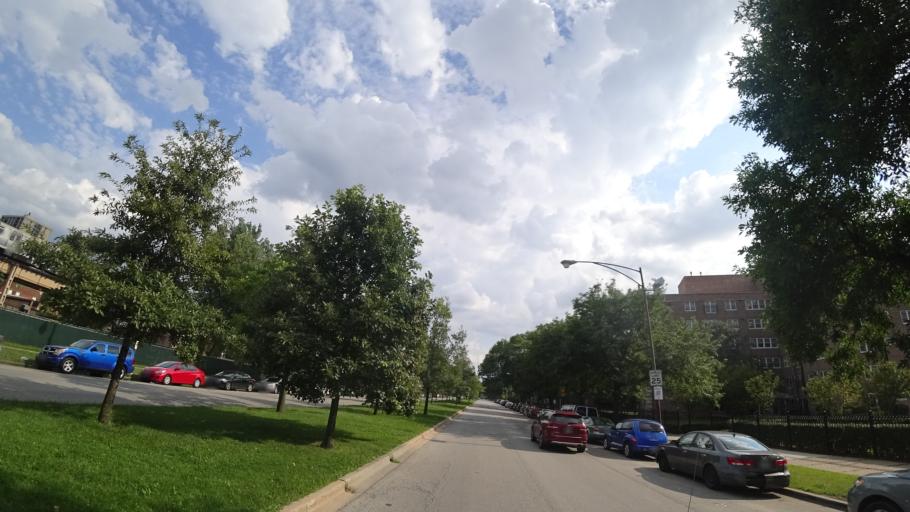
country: US
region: Illinois
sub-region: Cook County
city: Chicago
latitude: 41.8416
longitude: -87.6268
